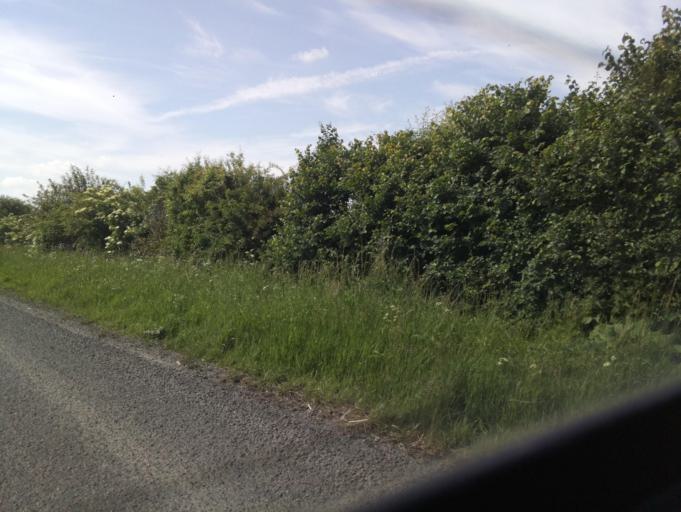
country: GB
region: England
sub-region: North Lincolnshire
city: Redbourne
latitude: 53.4338
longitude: -0.5503
